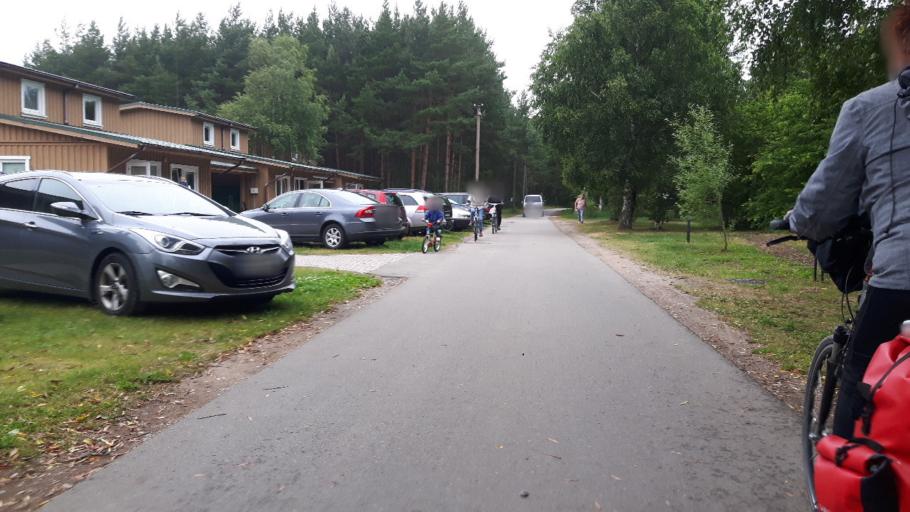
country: LT
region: Klaipedos apskritis
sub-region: Palanga
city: Sventoji
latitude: 56.0038
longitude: 21.0762
